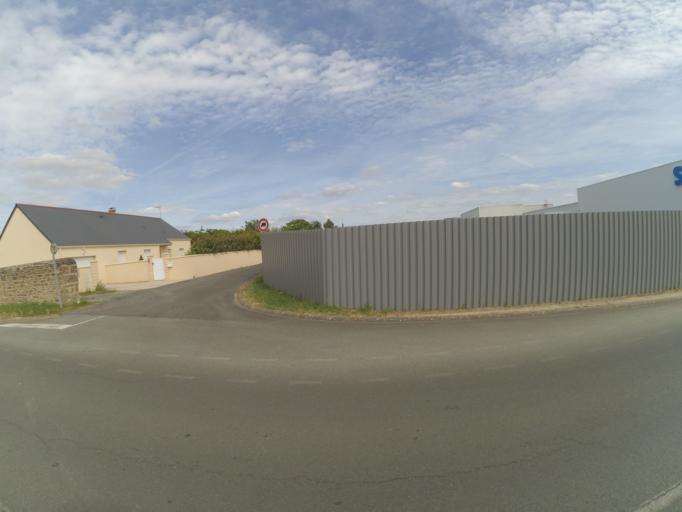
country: FR
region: Pays de la Loire
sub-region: Departement de Maine-et-Loire
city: Doue-la-Fontaine
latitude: 47.1921
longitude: -0.2896
